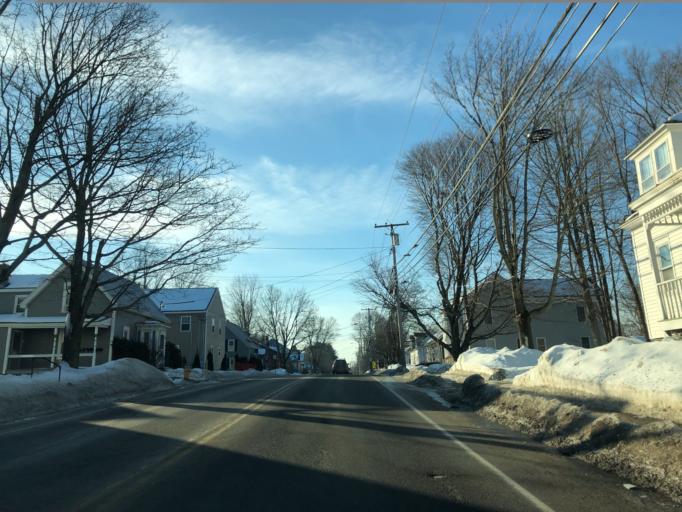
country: US
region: Maine
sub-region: Cumberland County
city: Westbrook
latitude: 43.6744
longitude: -70.3624
